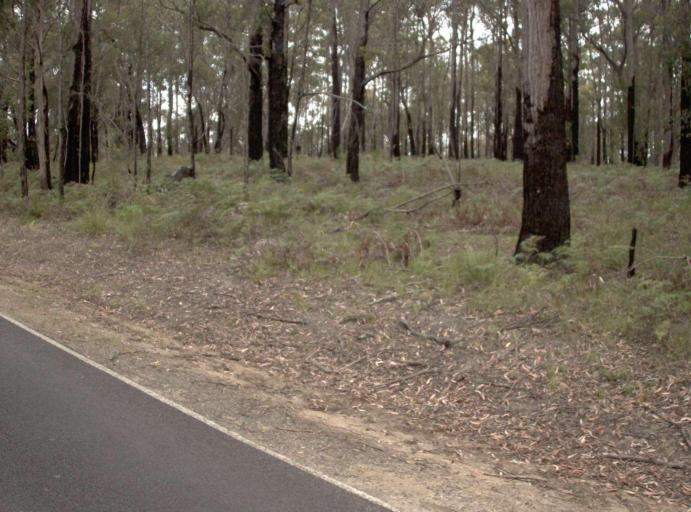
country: AU
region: Victoria
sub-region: Latrobe
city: Traralgon
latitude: -38.3927
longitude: 146.8101
